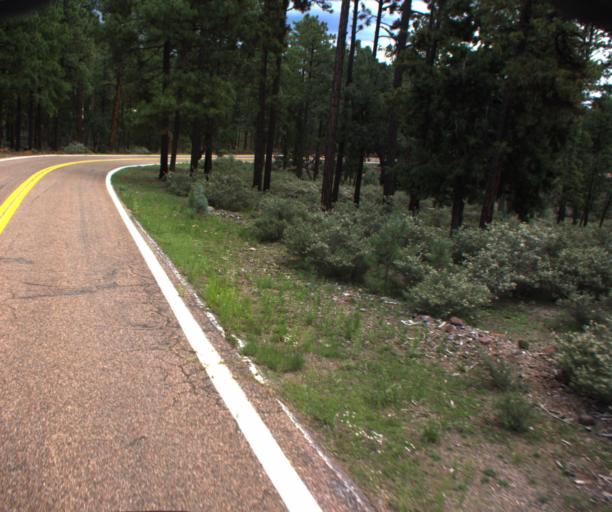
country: US
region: Arizona
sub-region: Greenlee County
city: Morenci
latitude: 33.5157
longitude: -109.3172
